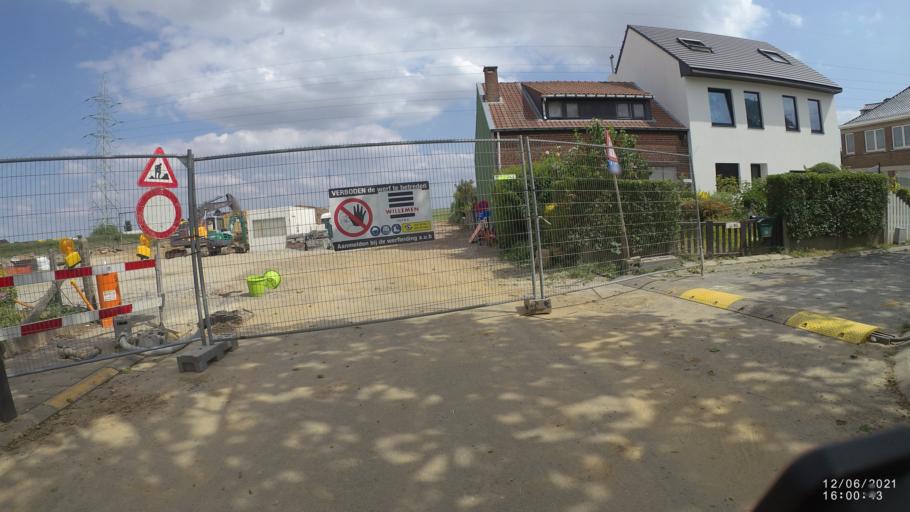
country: BE
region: Flanders
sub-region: Provincie Vlaams-Brabant
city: Asse
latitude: 50.8941
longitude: 4.2351
